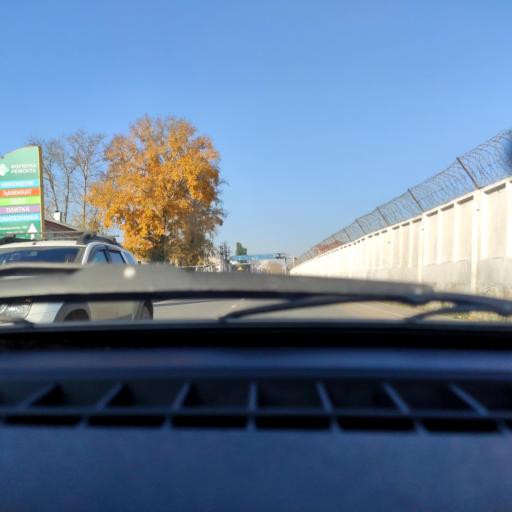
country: RU
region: Bashkortostan
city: Ufa
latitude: 54.7846
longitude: 56.0699
